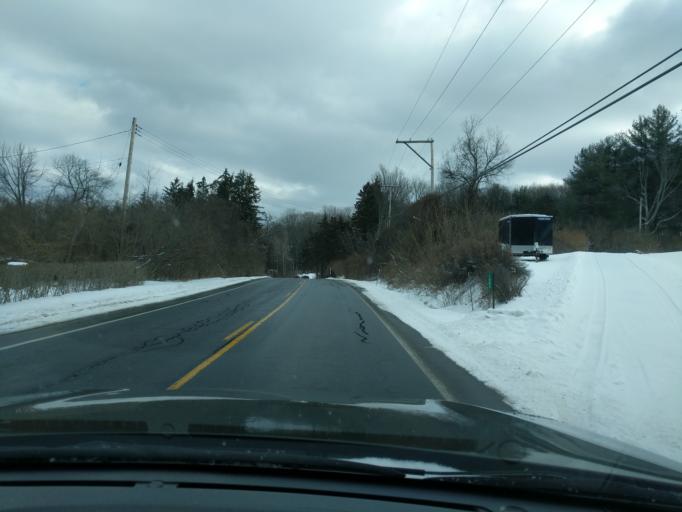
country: US
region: New York
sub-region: Tompkins County
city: Northeast Ithaca
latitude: 42.4272
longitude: -76.4111
